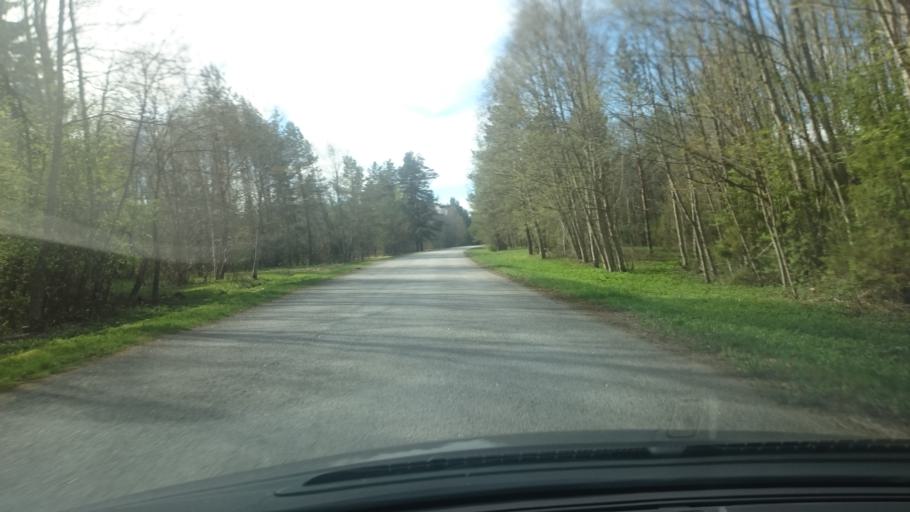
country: EE
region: Ida-Virumaa
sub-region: Sillamaee linn
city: Sillamae
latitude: 59.0842
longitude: 27.6739
